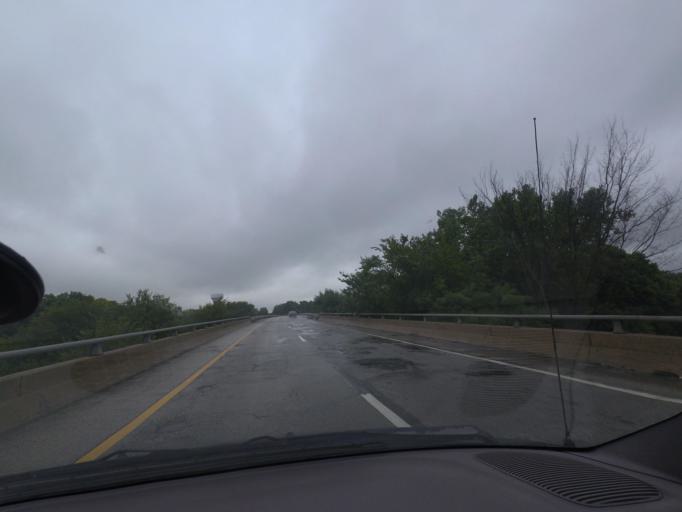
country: US
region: Illinois
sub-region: Champaign County
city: Champaign
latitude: 40.1189
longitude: -88.2862
